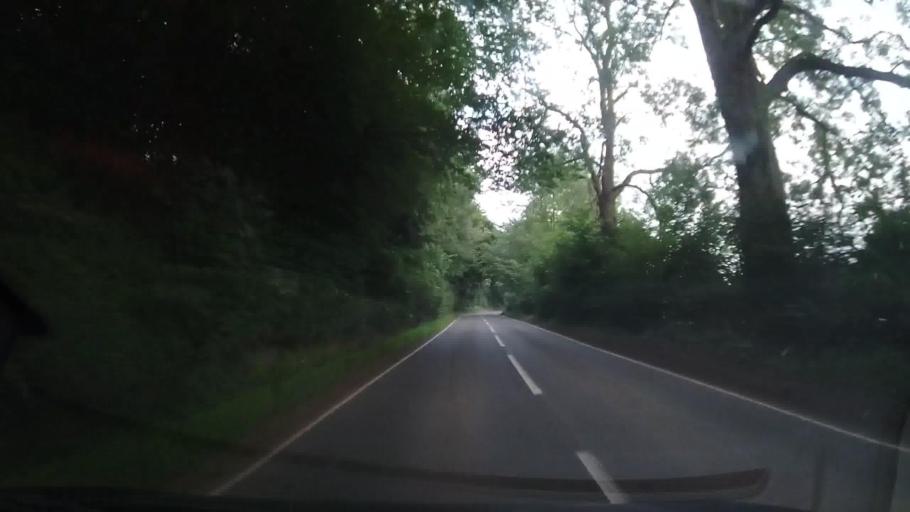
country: GB
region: Wales
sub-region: Sir Powys
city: Llanfechain
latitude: 52.8082
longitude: -3.1433
